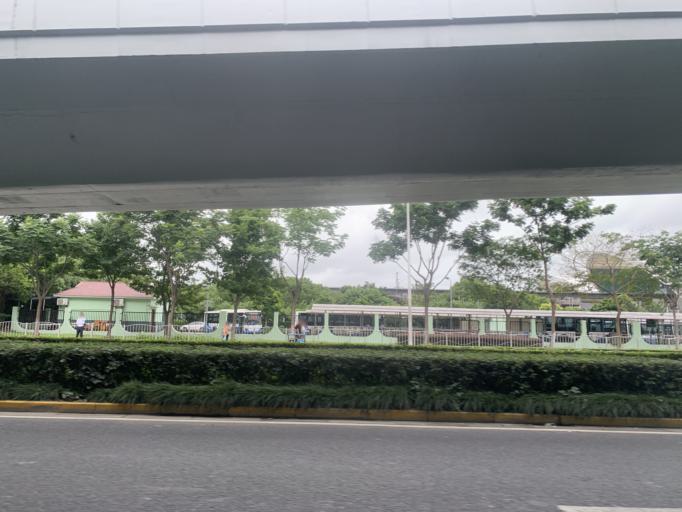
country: CN
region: Shanghai Shi
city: Huamu
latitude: 31.2056
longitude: 121.5559
